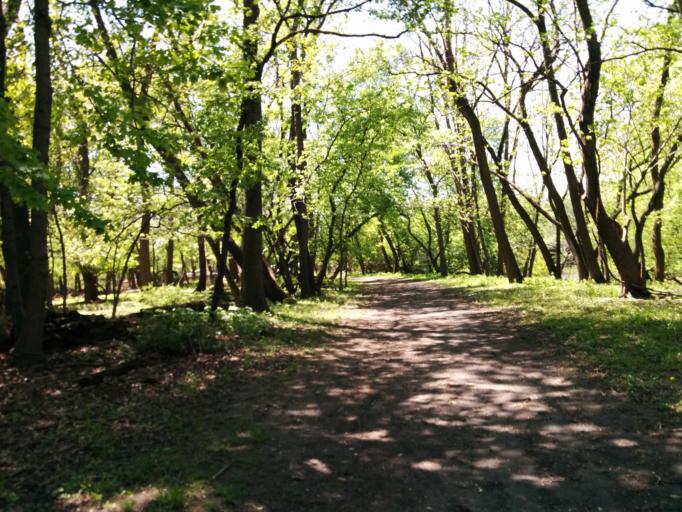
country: US
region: Illinois
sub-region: Cook County
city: Schiller Park
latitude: 41.9671
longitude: -87.8541
